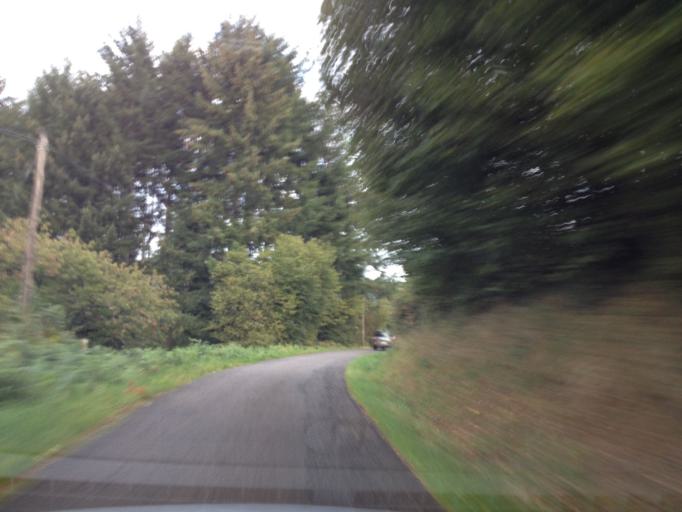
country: FR
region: Rhone-Alpes
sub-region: Departement de la Loire
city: Renaison
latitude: 46.0267
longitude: 3.8573
